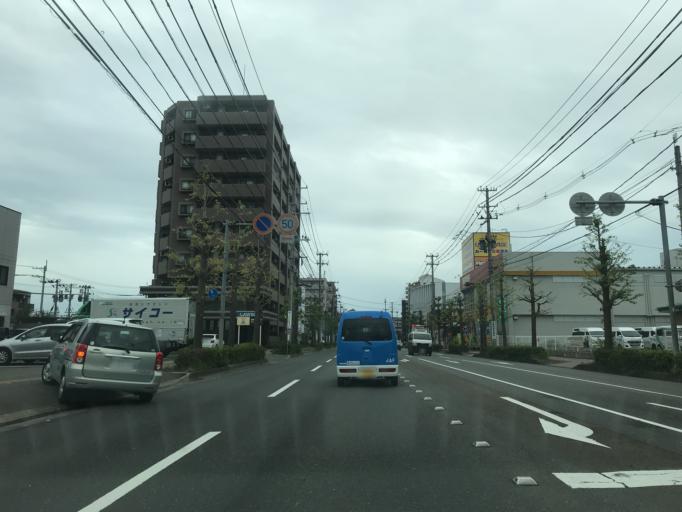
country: JP
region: Miyagi
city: Sendai-shi
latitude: 38.3105
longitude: 140.8917
